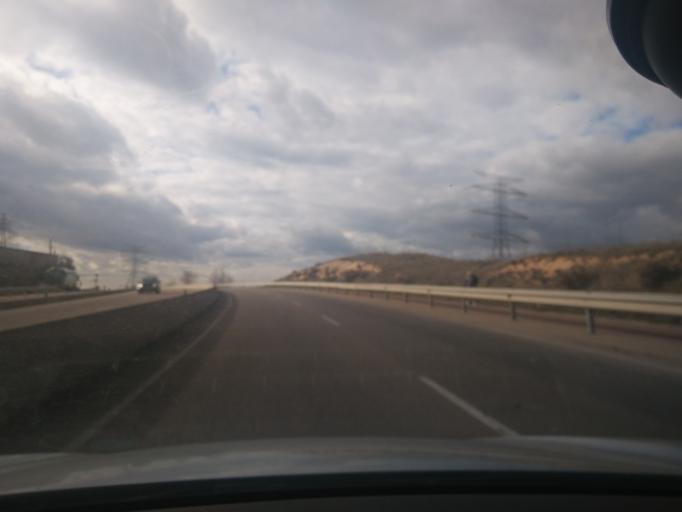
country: ES
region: Madrid
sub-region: Provincia de Madrid
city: Alcobendas
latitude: 40.5535
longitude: -3.6773
